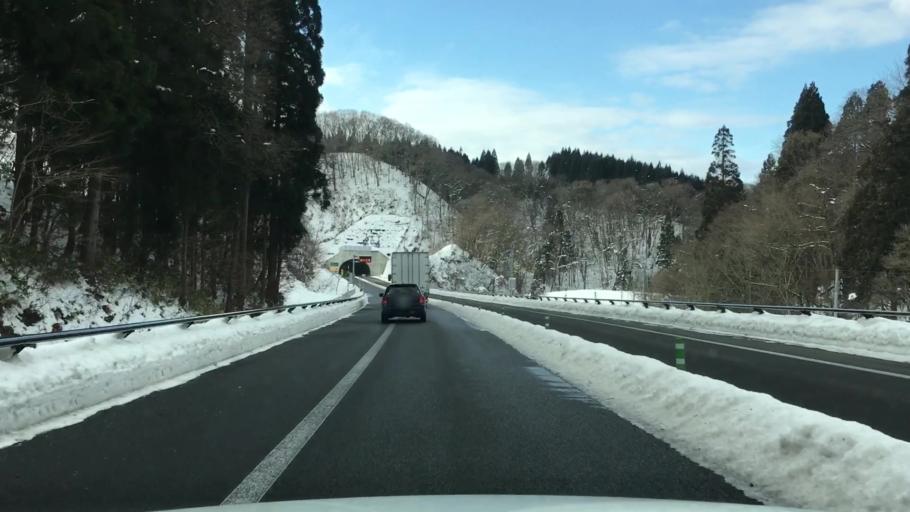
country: JP
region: Akita
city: Takanosu
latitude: 40.2245
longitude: 140.4338
